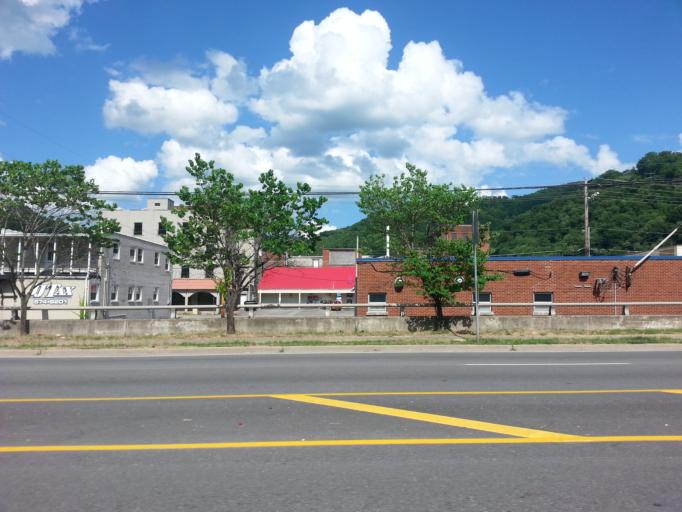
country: US
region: Kentucky
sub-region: Harlan County
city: Harlan
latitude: 36.8462
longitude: -83.3245
